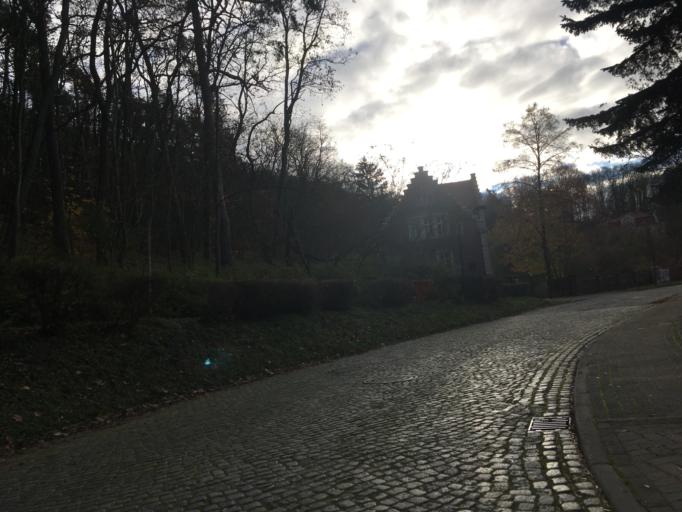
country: DE
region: Brandenburg
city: Buckow
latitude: 52.5632
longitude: 14.0771
